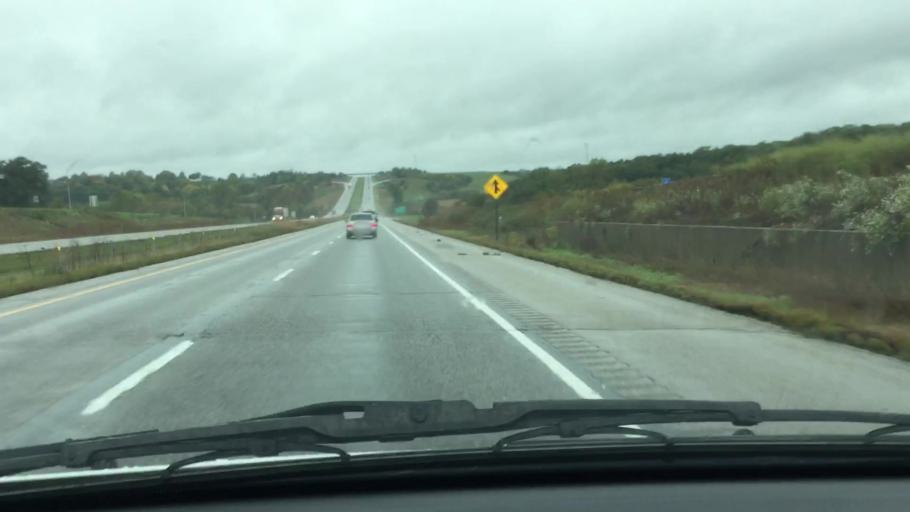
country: US
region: Iowa
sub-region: Poweshiek County
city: Grinnell
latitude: 41.6955
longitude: -92.7731
